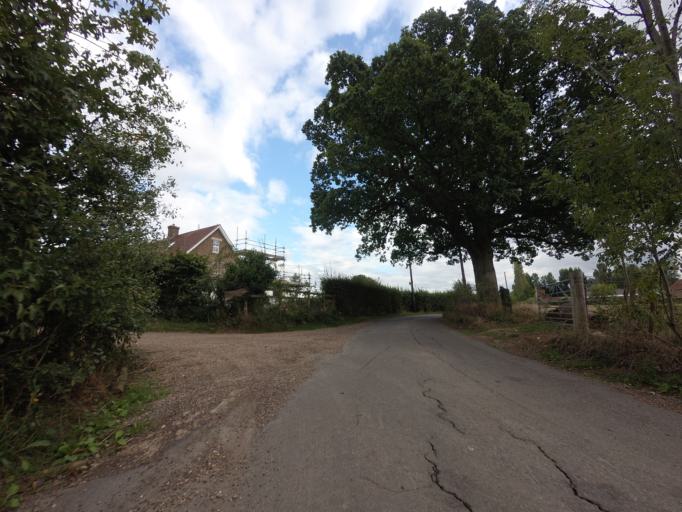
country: GB
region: England
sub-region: Kent
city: Staplehurst
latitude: 51.2093
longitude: 0.5340
